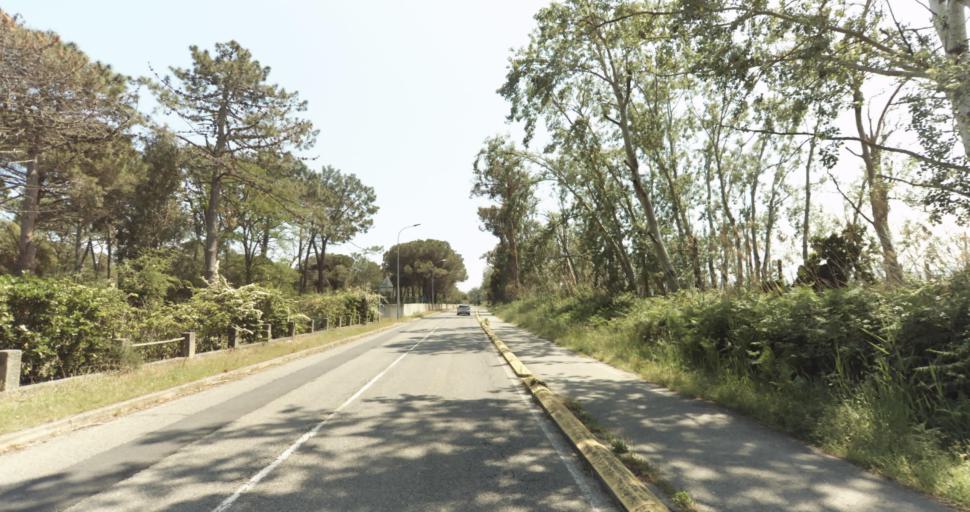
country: FR
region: Corsica
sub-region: Departement de la Haute-Corse
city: Biguglia
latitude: 42.6350
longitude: 9.4623
